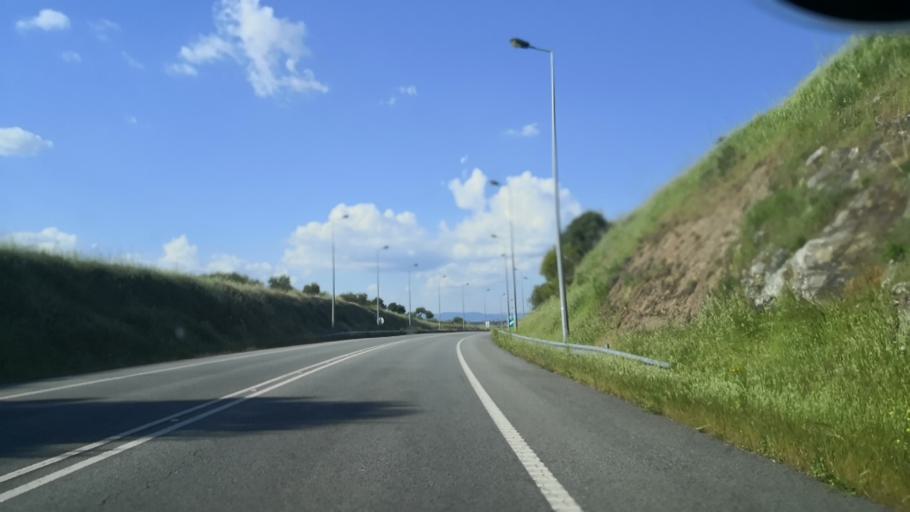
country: PT
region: Portalegre
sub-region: Arronches
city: Arronches
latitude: 39.0512
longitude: -7.4464
